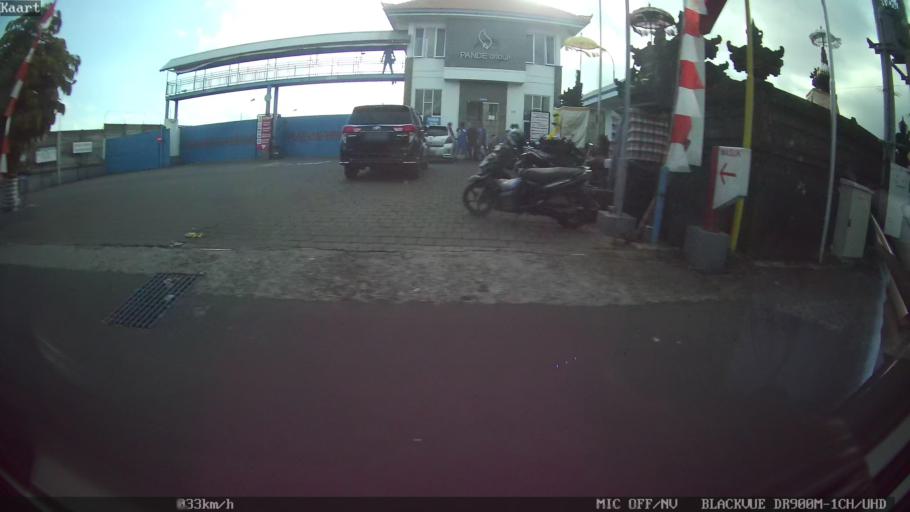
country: ID
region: Bali
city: Banjar Sedang
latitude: -8.5632
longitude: 115.2343
